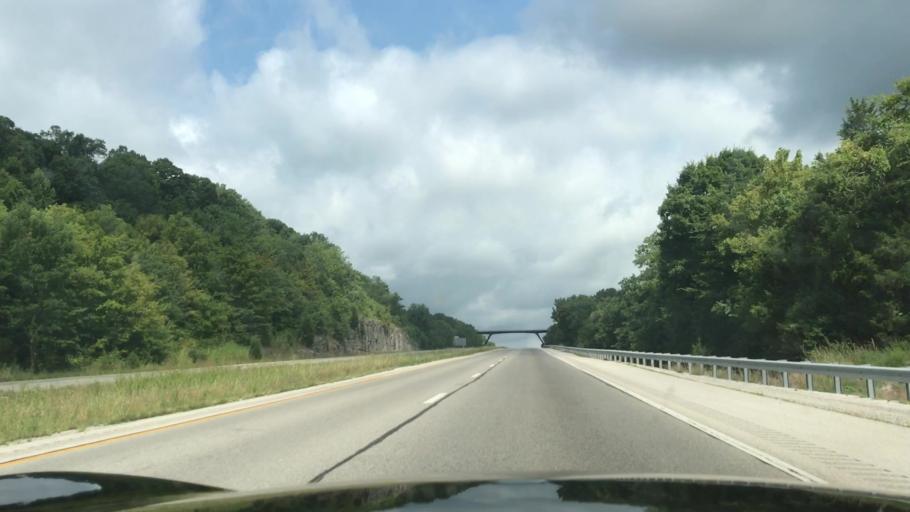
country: US
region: Kentucky
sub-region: Warren County
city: Bowling Green
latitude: 37.0153
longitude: -86.5183
